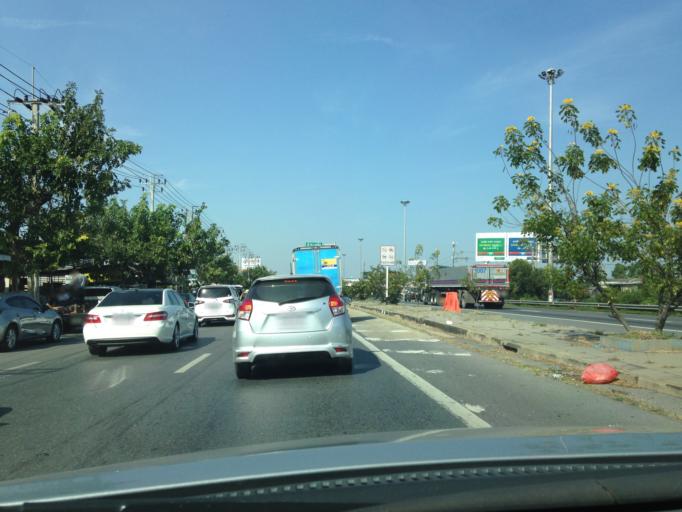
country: TH
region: Nonthaburi
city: Bang Yai
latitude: 13.8275
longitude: 100.4127
